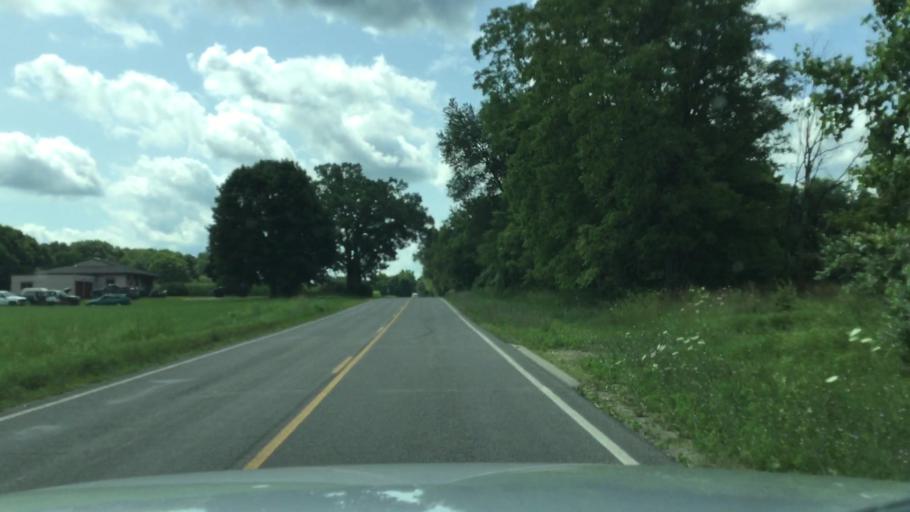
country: US
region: Michigan
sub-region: Montcalm County
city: Greenville
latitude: 43.1536
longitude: -85.2136
